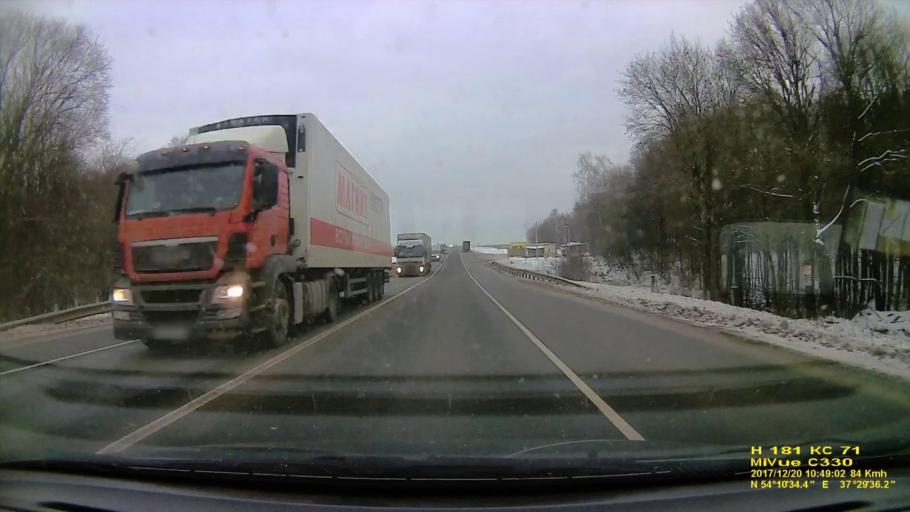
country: RU
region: Tula
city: Kosaya Gora
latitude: 54.1764
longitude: 37.4933
